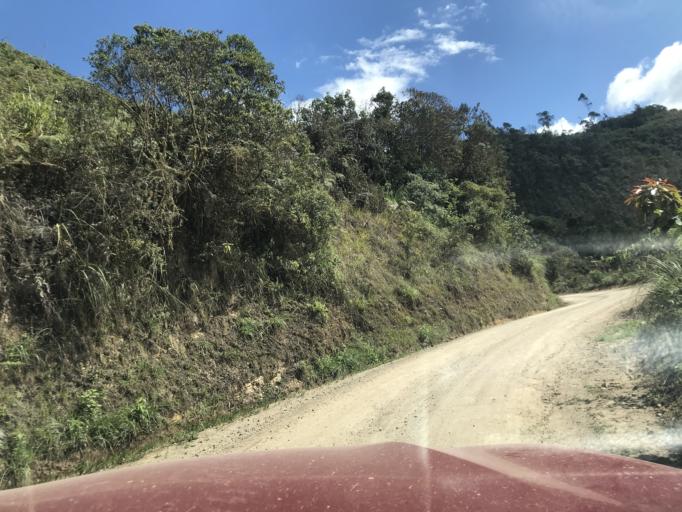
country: PE
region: Cajamarca
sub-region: Provincia de Chota
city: Querocoto
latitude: -6.3491
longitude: -79.0363
